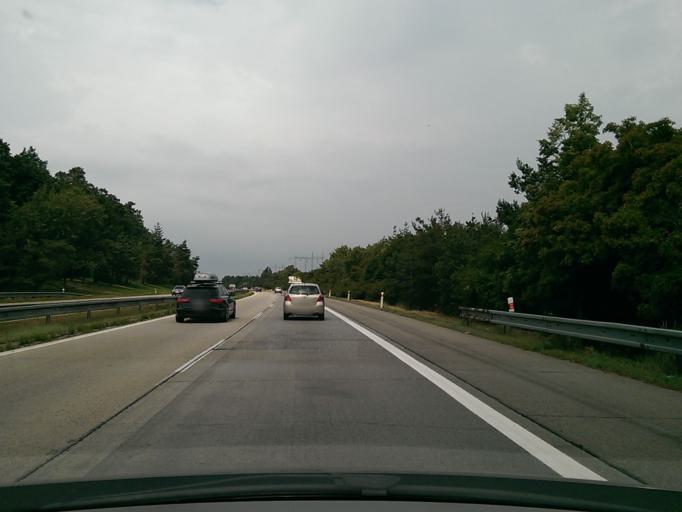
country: CZ
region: South Moravian
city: Ricany
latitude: 49.2422
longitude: 16.3684
